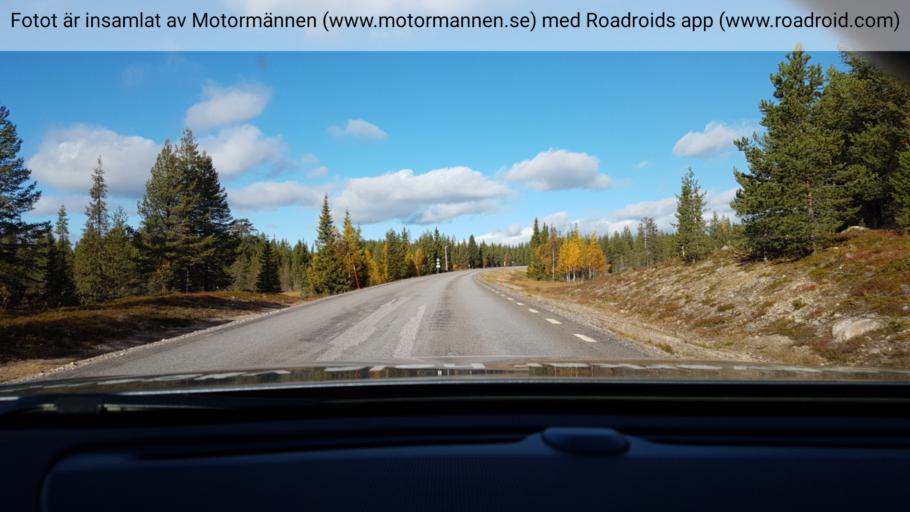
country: SE
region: Norrbotten
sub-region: Arjeplogs Kommun
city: Arjeplog
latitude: 65.8925
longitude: 18.3714
